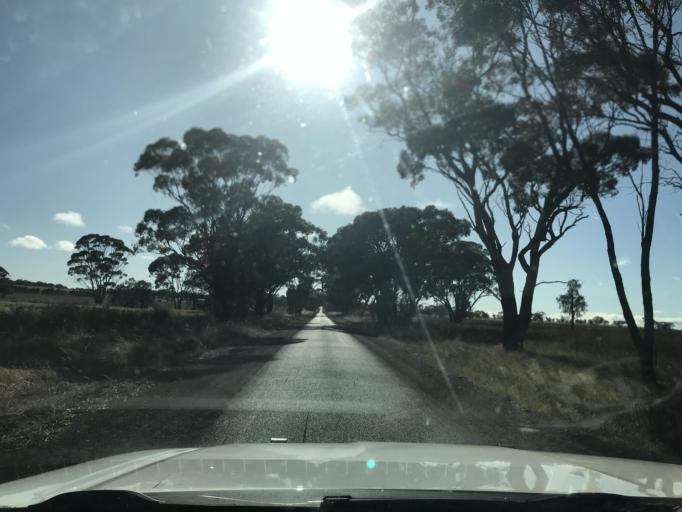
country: AU
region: Victoria
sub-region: Horsham
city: Horsham
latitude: -36.6985
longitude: 141.6092
